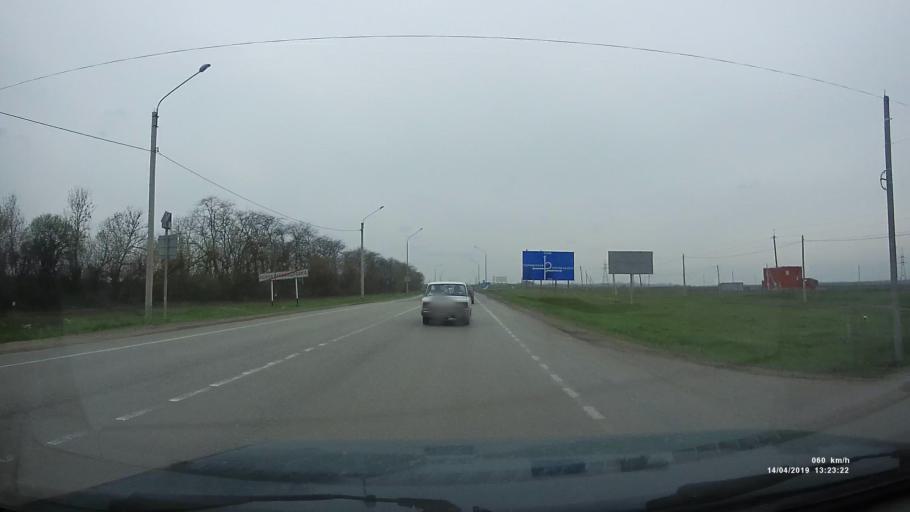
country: RU
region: Rostov
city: Kuleshovka
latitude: 47.0835
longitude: 39.5011
